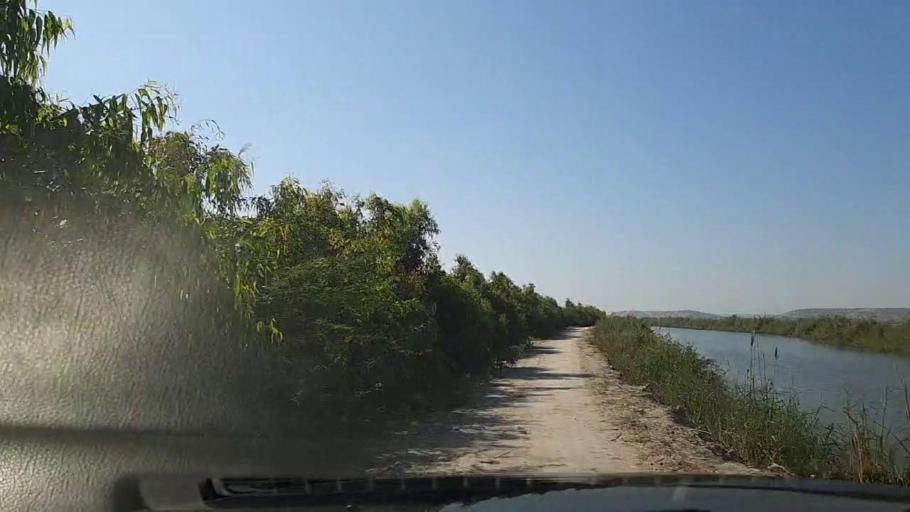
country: PK
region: Sindh
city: Thatta
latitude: 24.6937
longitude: 67.8953
